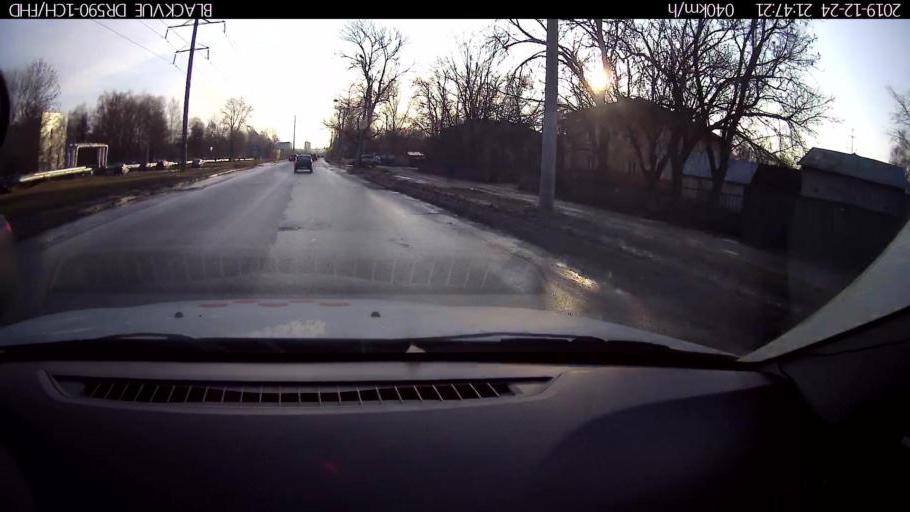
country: RU
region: Nizjnij Novgorod
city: Gorbatovka
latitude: 56.2306
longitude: 43.8396
